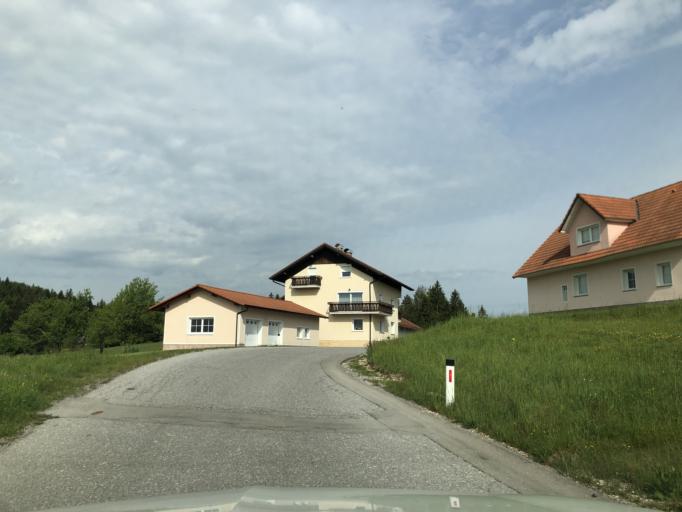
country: SI
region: Bloke
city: Nova Vas
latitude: 45.7970
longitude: 14.5410
